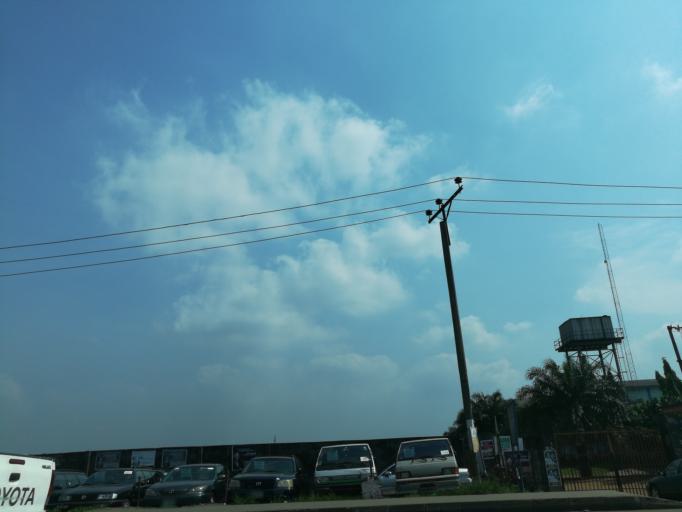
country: NG
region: Rivers
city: Port Harcourt
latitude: 4.8072
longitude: 6.9871
